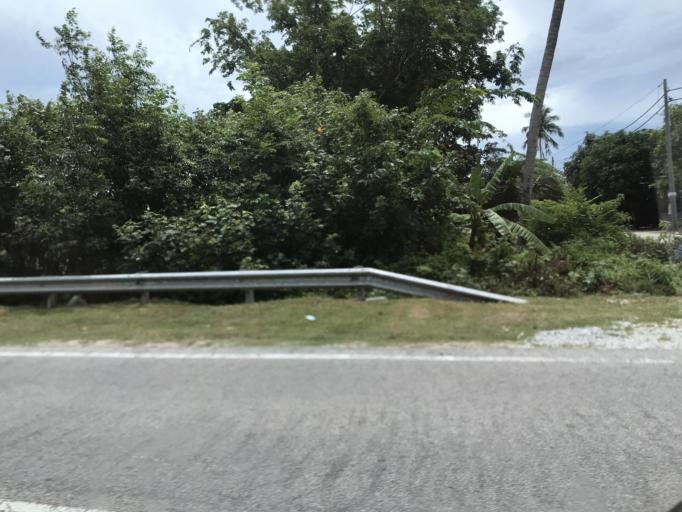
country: MY
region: Kelantan
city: Tumpat
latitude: 6.1737
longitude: 102.2058
